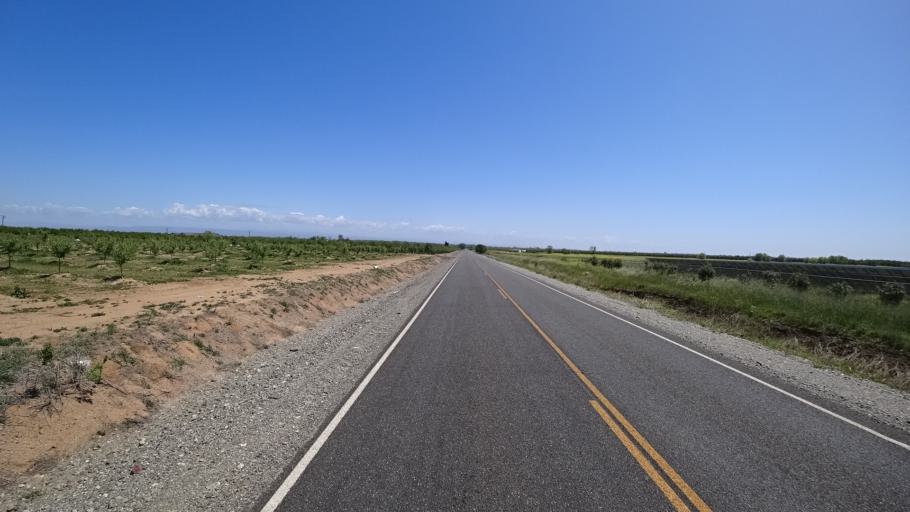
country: US
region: California
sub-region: Glenn County
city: Hamilton City
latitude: 39.7665
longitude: -122.0489
